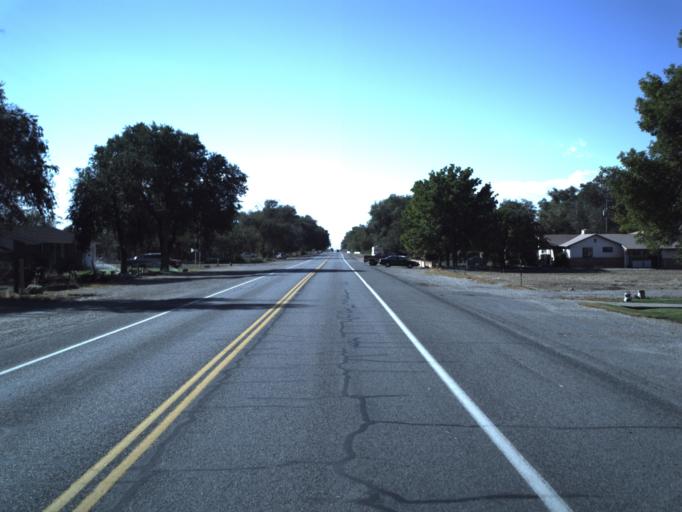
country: US
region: Utah
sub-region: Millard County
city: Delta
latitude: 39.2913
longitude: -112.6527
